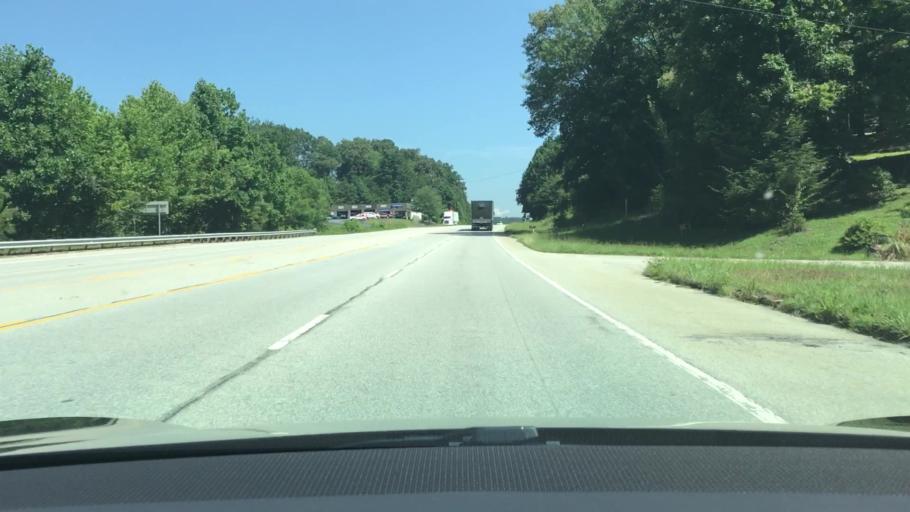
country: US
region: Georgia
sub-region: Rabun County
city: Mountain City
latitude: 35.0002
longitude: -83.3827
